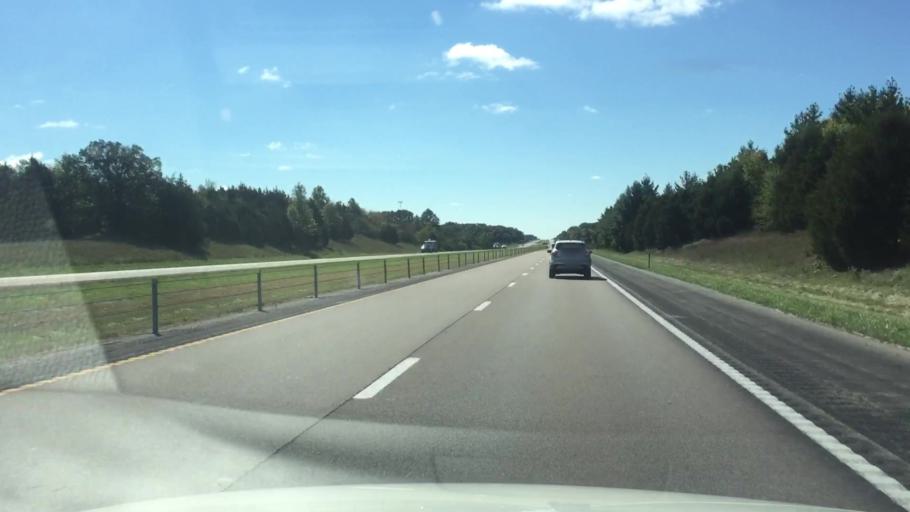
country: US
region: Missouri
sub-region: Boone County
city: Ashland
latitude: 38.7389
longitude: -92.2539
